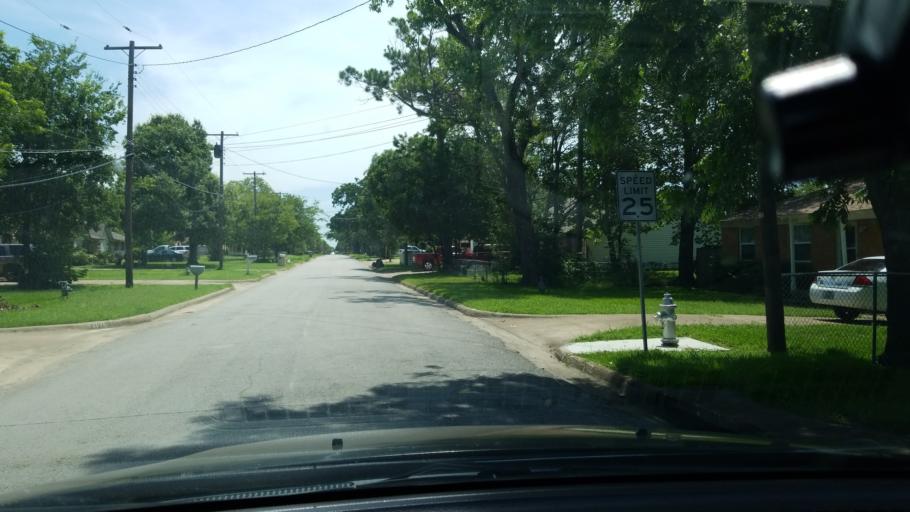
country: US
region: Texas
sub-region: Dallas County
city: Balch Springs
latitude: 32.7524
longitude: -96.6309
